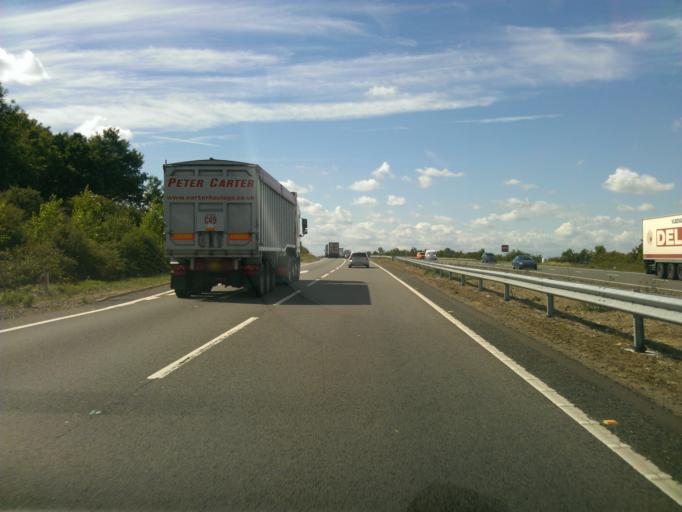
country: GB
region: England
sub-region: Bedford
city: Pertenhall
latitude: 52.3517
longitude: -0.3745
